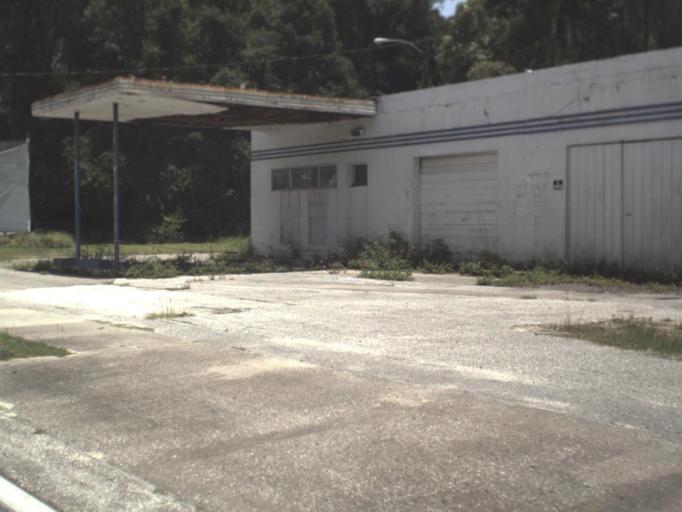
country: US
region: Florida
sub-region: Levy County
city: Manatee Road
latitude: 29.5910
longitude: -82.9323
